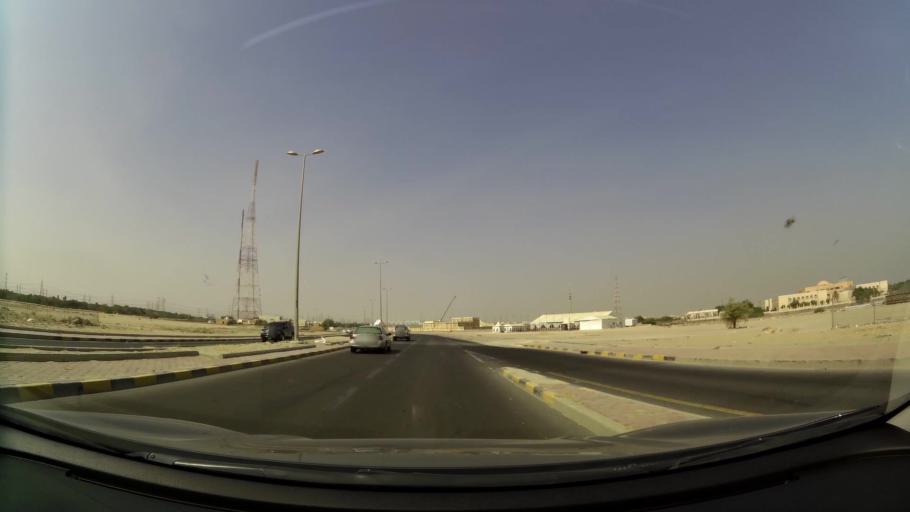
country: KW
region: Al Ahmadi
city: Al Fahahil
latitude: 29.0772
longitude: 48.1079
